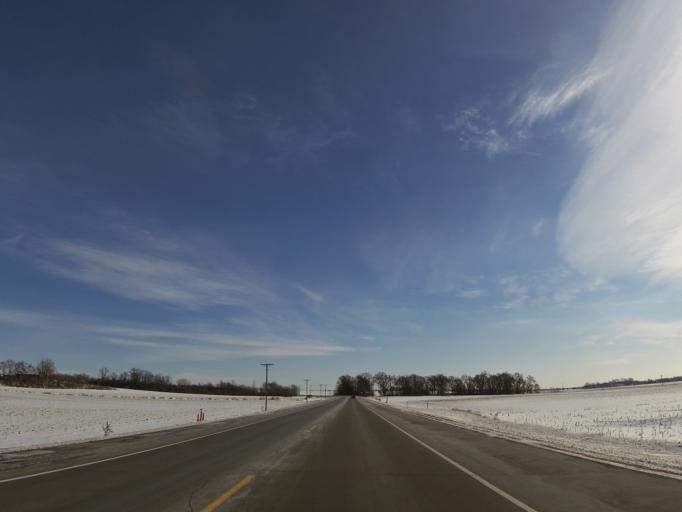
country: US
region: Minnesota
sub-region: Washington County
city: Saint Paul Park
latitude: 44.7386
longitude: -93.0006
